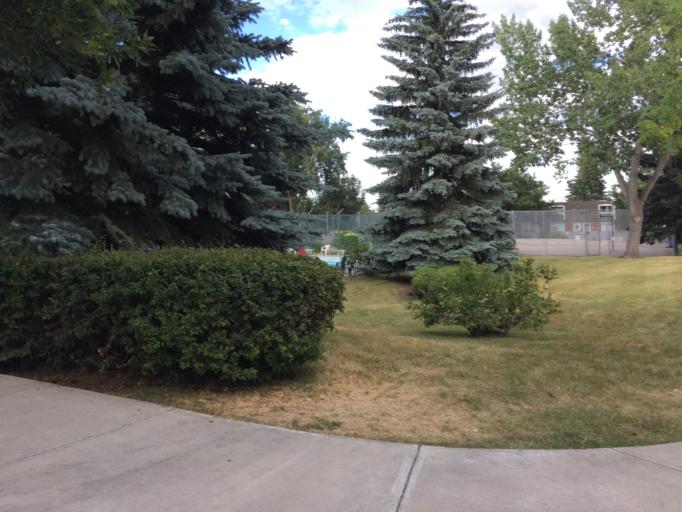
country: CA
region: Alberta
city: Calgary
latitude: 50.9488
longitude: -114.0830
